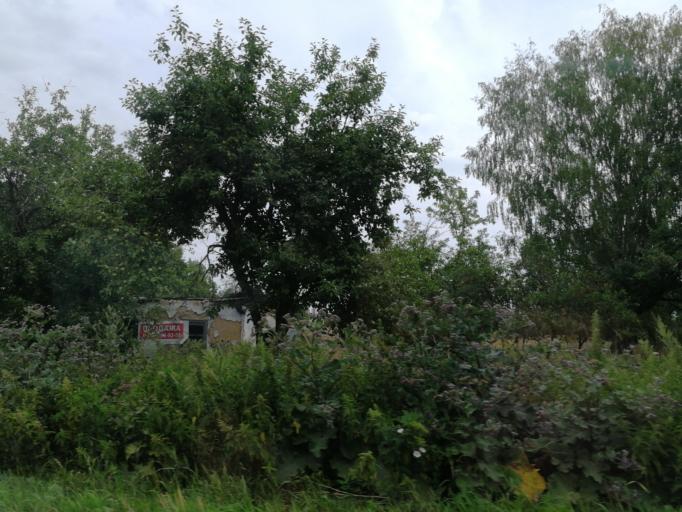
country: RU
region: Tula
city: Tovarkovskiy
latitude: 53.6840
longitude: 38.1954
